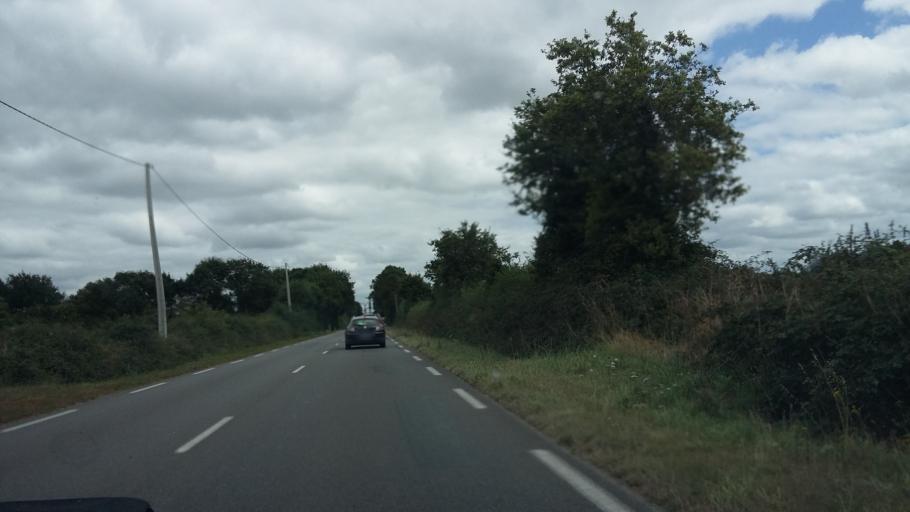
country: FR
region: Pays de la Loire
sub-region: Departement de la Vendee
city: Challans
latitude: 46.8341
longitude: -1.8277
